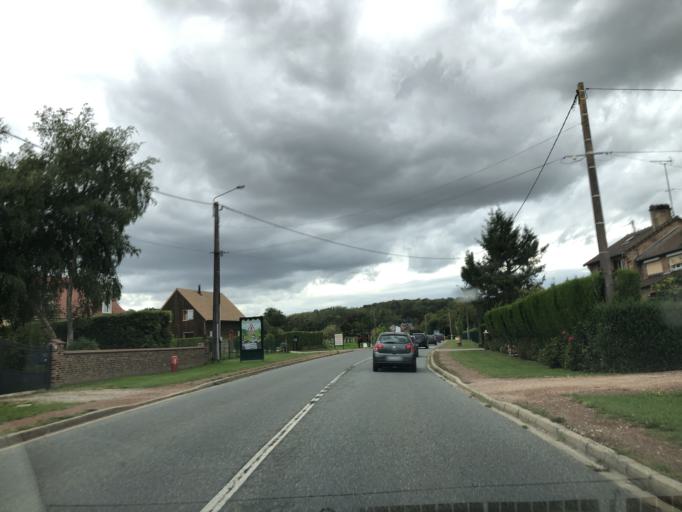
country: FR
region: Picardie
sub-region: Departement de la Somme
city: Abbeville
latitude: 50.1088
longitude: 1.7750
